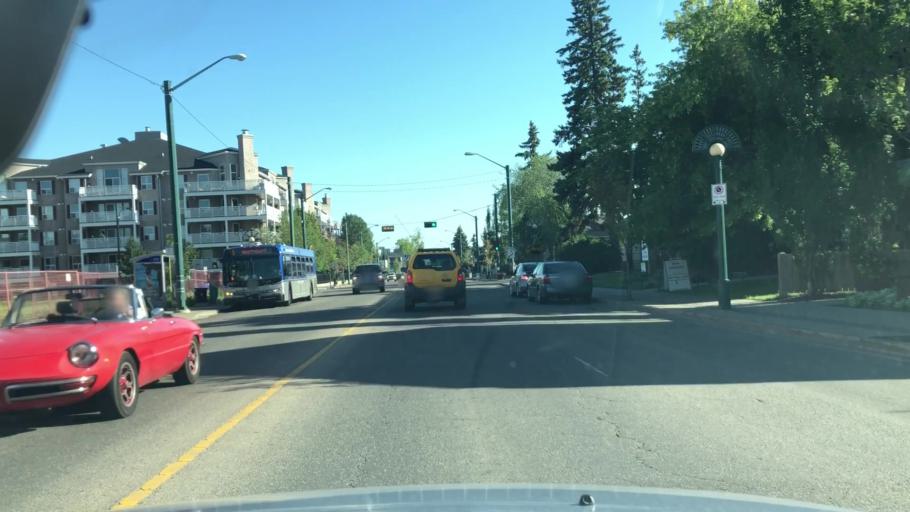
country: CA
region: Alberta
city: Edmonton
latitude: 53.5564
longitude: -113.5359
